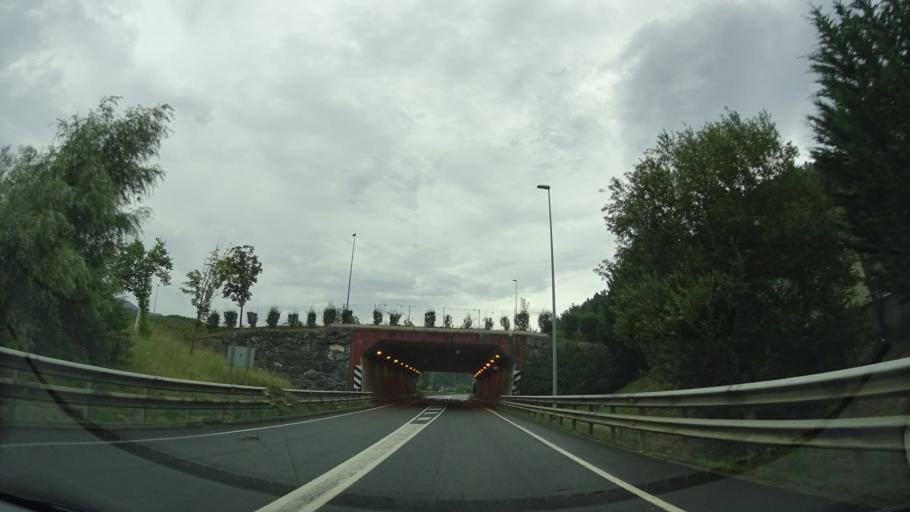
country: ES
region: Basque Country
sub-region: Bizkaia
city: Areatza
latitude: 43.1656
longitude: -2.7695
